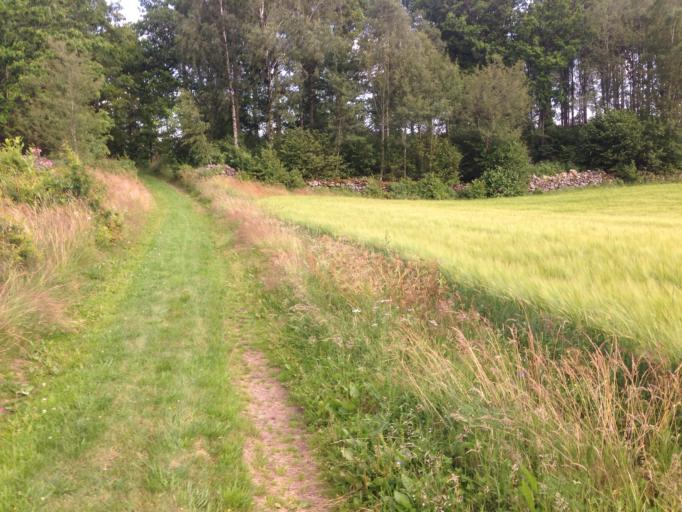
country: SE
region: Kronoberg
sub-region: Ljungby Kommun
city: Ljungby
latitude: 56.8633
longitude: 13.7823
